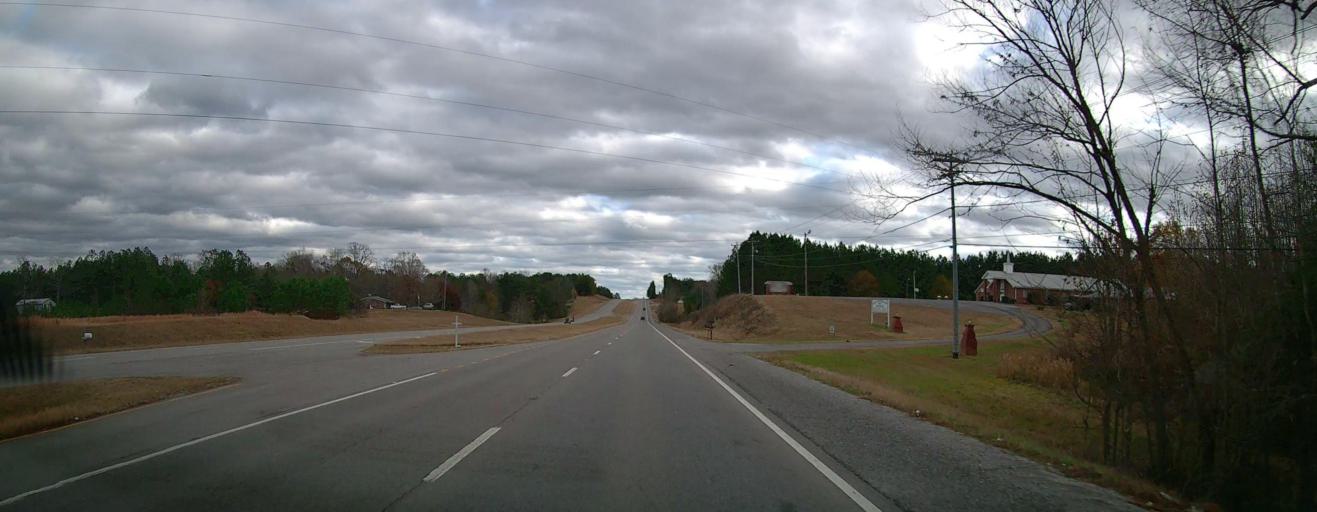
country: US
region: Alabama
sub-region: Lawrence County
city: Town Creek
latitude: 34.5835
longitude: -87.4151
